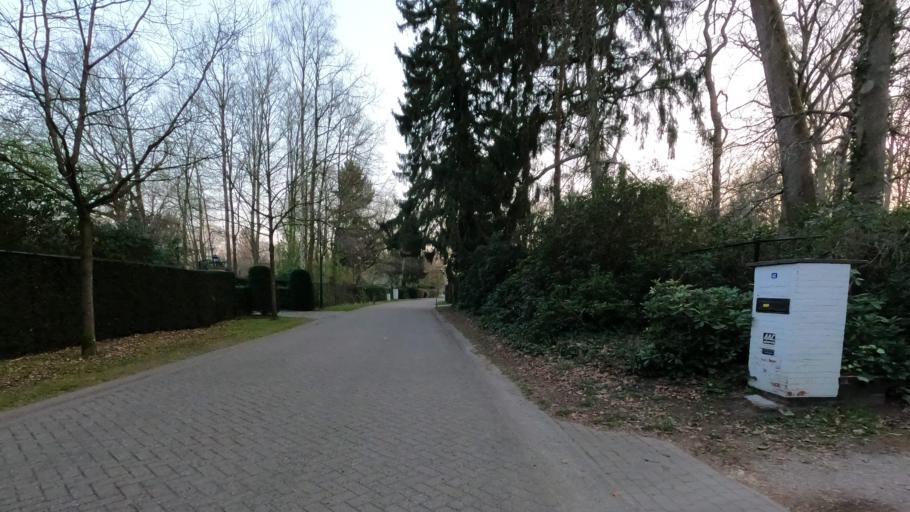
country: BE
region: Flanders
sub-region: Provincie Antwerpen
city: Schilde
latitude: 51.2562
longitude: 4.5761
